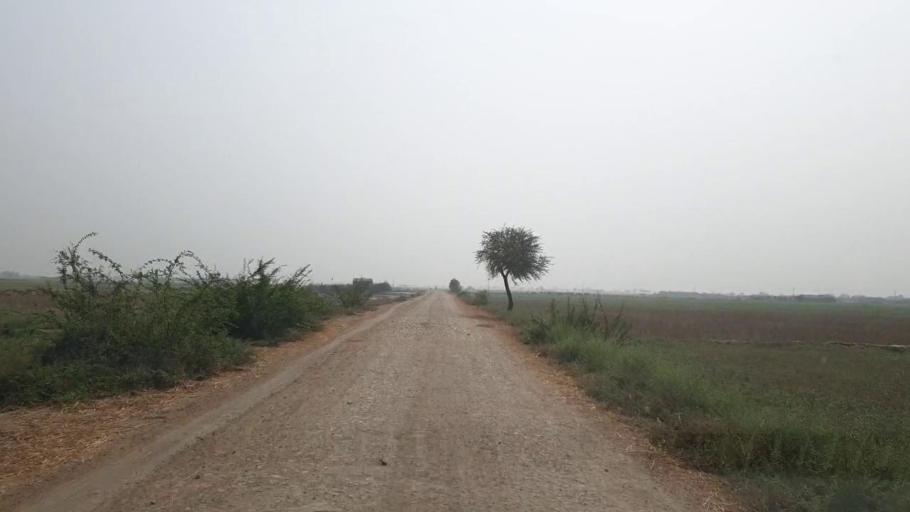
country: PK
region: Sindh
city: Kario
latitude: 24.6519
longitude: 68.5956
